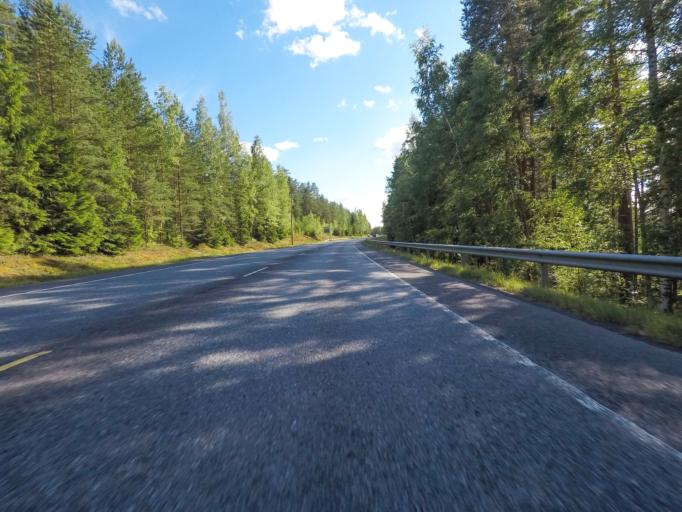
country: FI
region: Uusimaa
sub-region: Helsinki
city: Vihti
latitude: 60.3340
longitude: 24.2880
